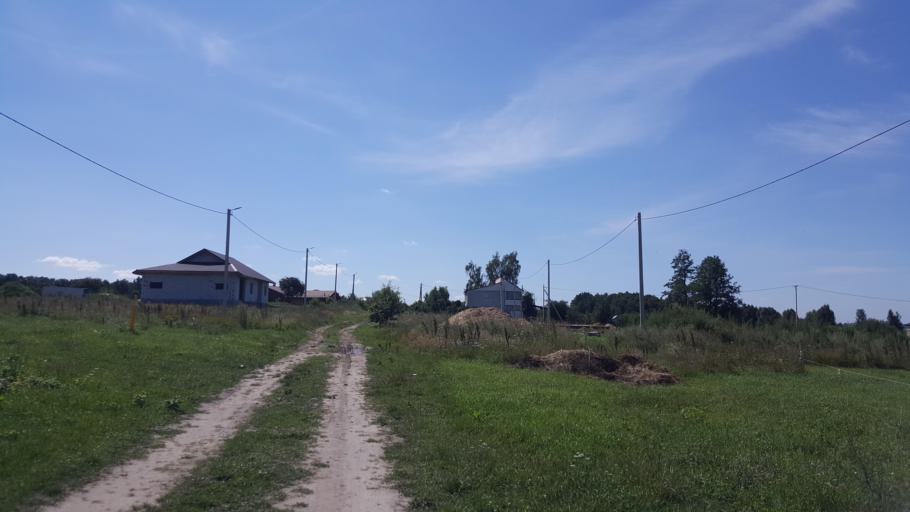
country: BY
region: Brest
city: Charnawchytsy
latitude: 52.2674
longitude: 23.7596
